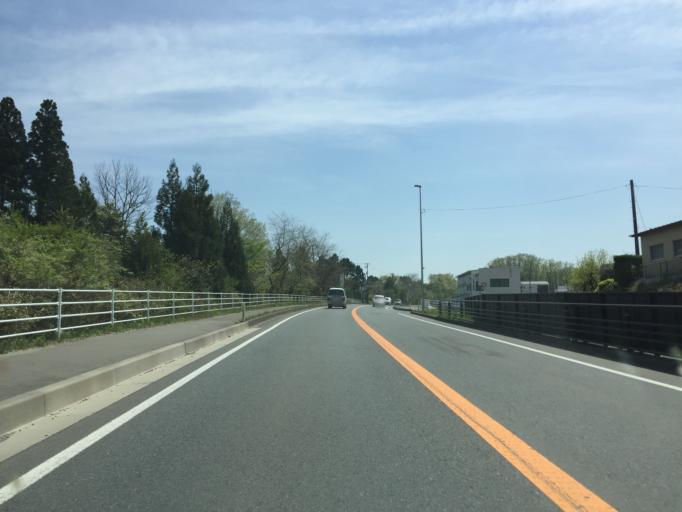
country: JP
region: Miyagi
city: Marumori
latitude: 37.8655
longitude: 140.9204
